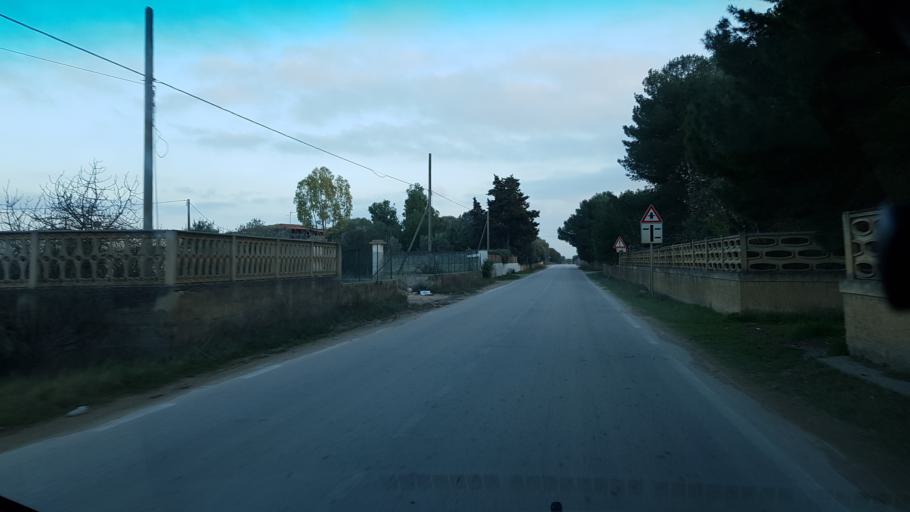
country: IT
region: Apulia
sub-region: Provincia di Brindisi
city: San Vito dei Normanni
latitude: 40.6435
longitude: 17.7777
